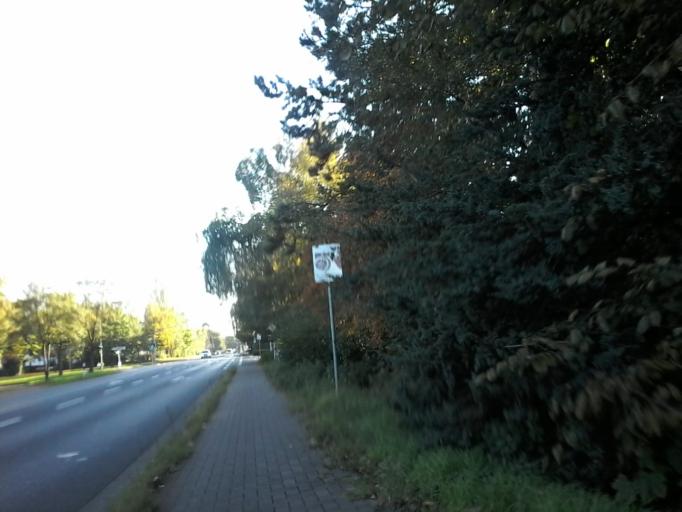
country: DE
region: Lower Saxony
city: Achim
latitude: 53.0214
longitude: 9.0314
